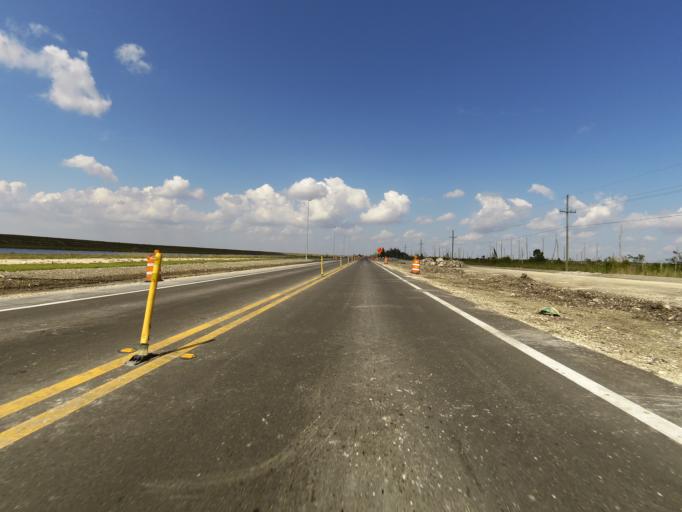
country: US
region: Florida
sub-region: Miami-Dade County
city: Palm Springs North
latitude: 25.9098
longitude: -80.4685
